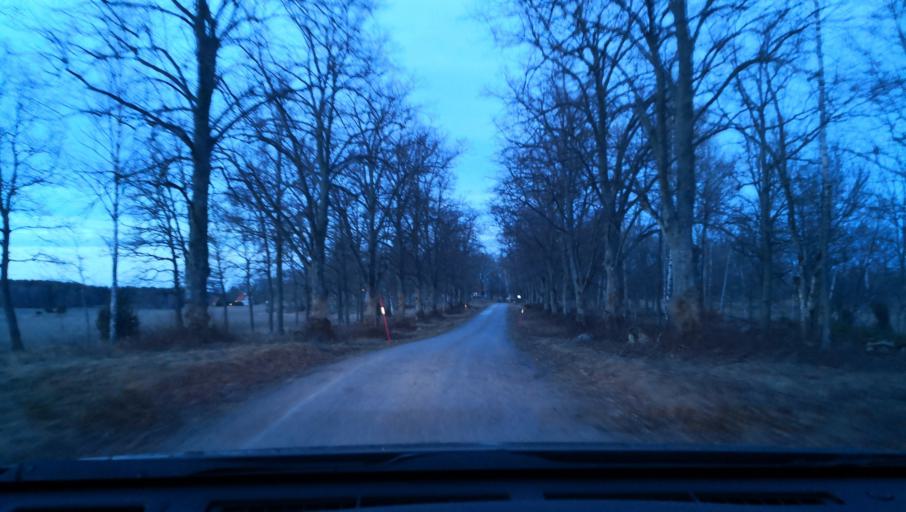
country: SE
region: Uppsala
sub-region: Enkopings Kommun
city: Dalby
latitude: 59.5525
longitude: 17.3688
